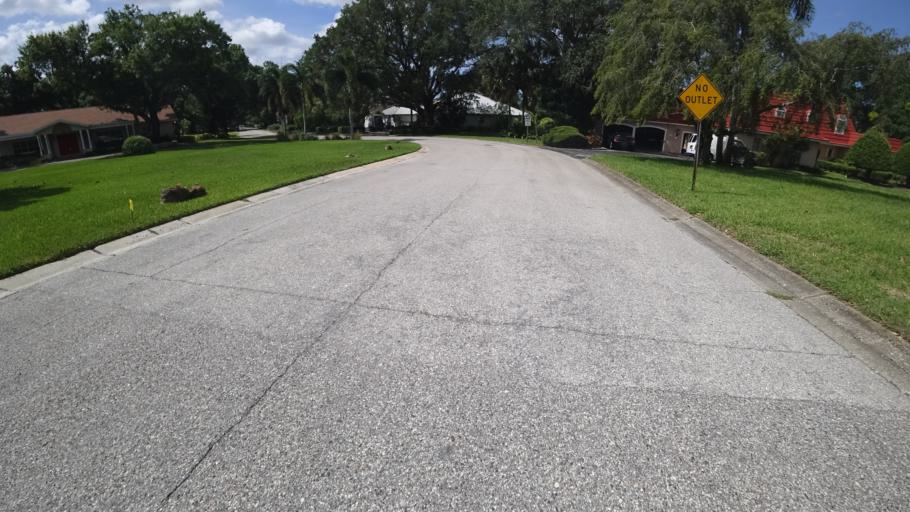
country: US
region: Florida
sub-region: Manatee County
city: West Bradenton
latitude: 27.5054
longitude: -82.6121
